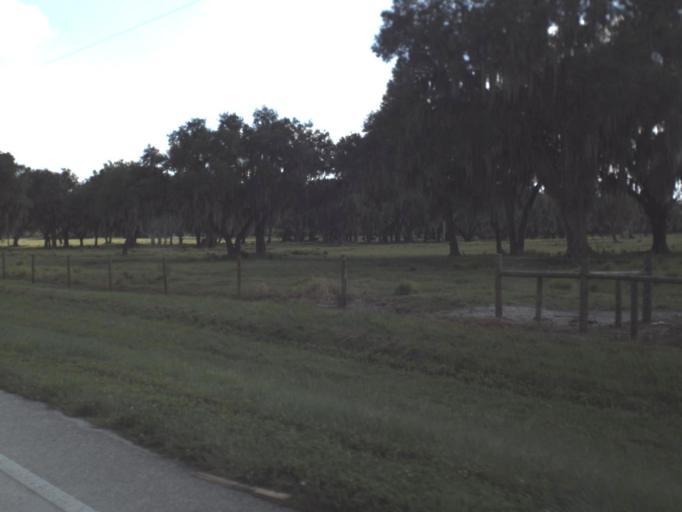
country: US
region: Florida
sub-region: Hardee County
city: Zolfo Springs
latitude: 27.4576
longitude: -81.6702
